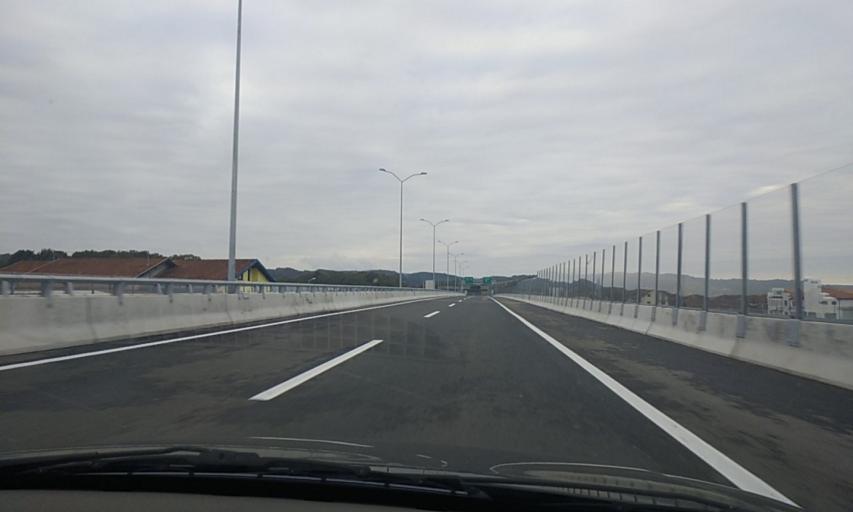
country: BA
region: Republika Srpska
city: Laktasi
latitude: 44.9185
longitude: 17.3130
